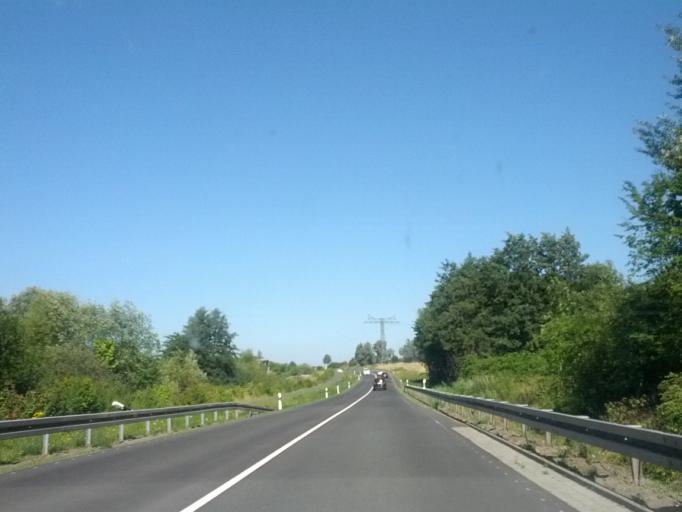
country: DE
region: Mecklenburg-Vorpommern
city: Sagard
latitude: 54.4980
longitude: 13.5641
